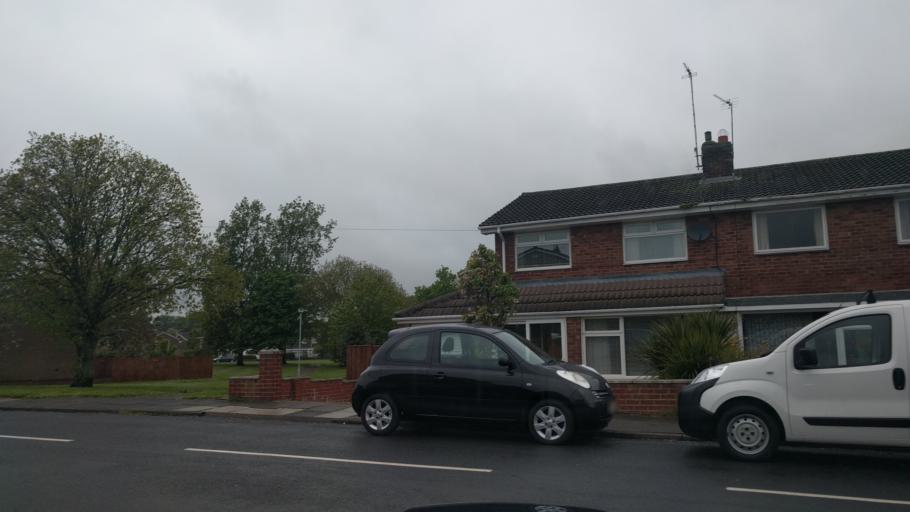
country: GB
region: England
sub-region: Northumberland
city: Morpeth
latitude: 55.1623
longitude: -1.7022
